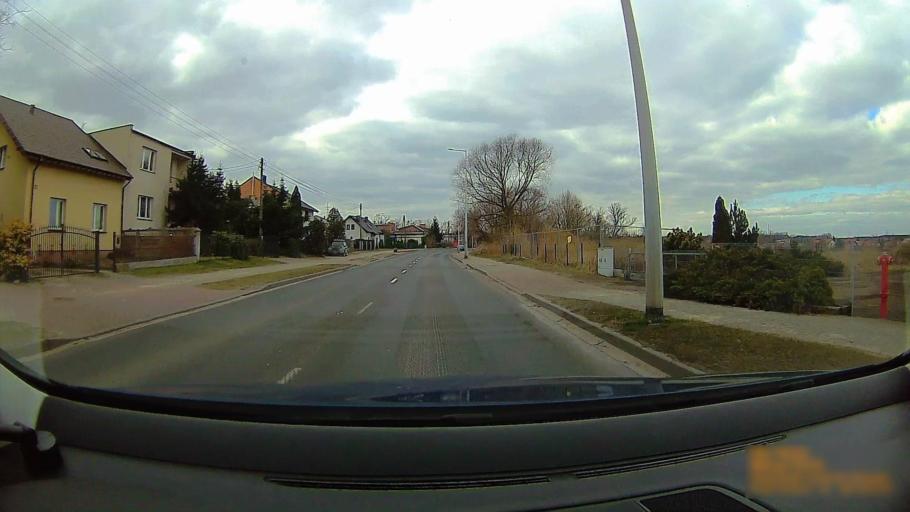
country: PL
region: Greater Poland Voivodeship
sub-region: Konin
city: Konin
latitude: 52.2029
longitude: 18.2381
